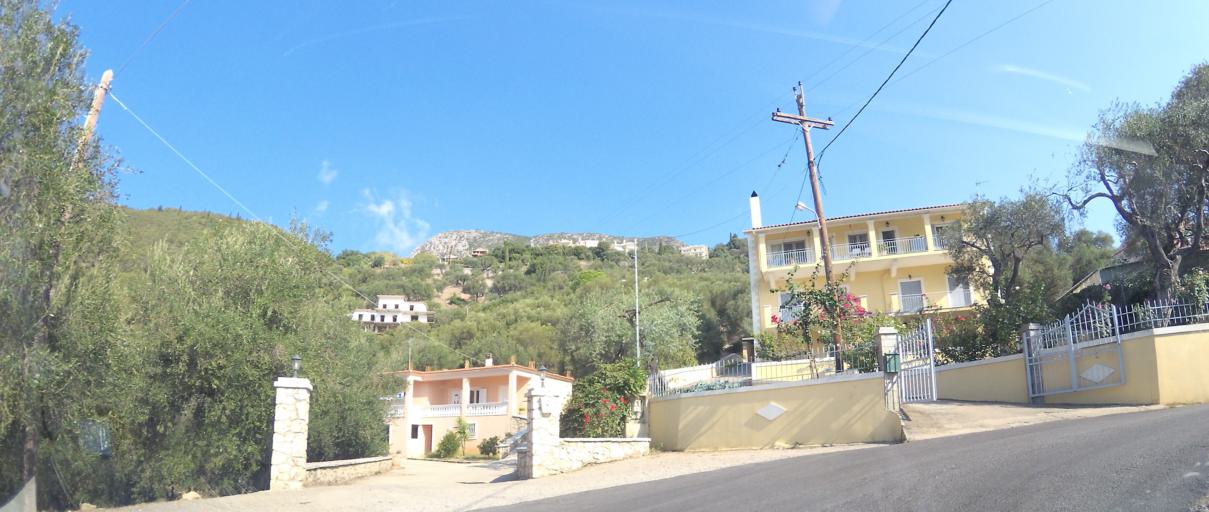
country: GR
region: Ionian Islands
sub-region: Nomos Kerkyras
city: Kontokali
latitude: 39.7156
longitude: 19.8454
